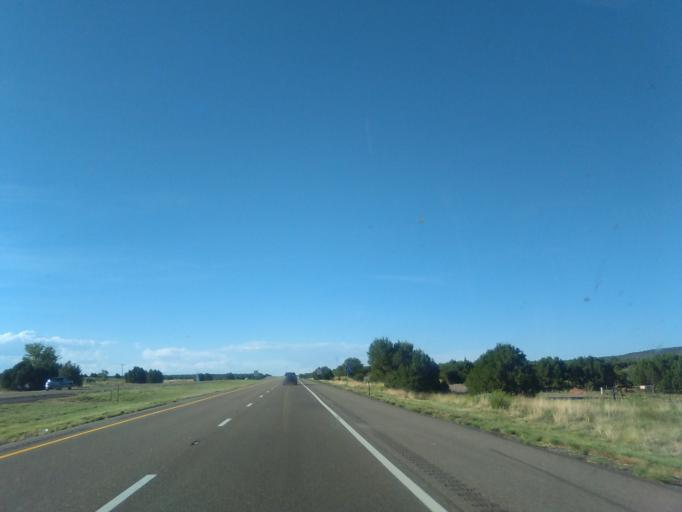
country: US
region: New Mexico
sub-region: San Miguel County
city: Las Vegas
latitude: 35.4648
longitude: -105.2763
